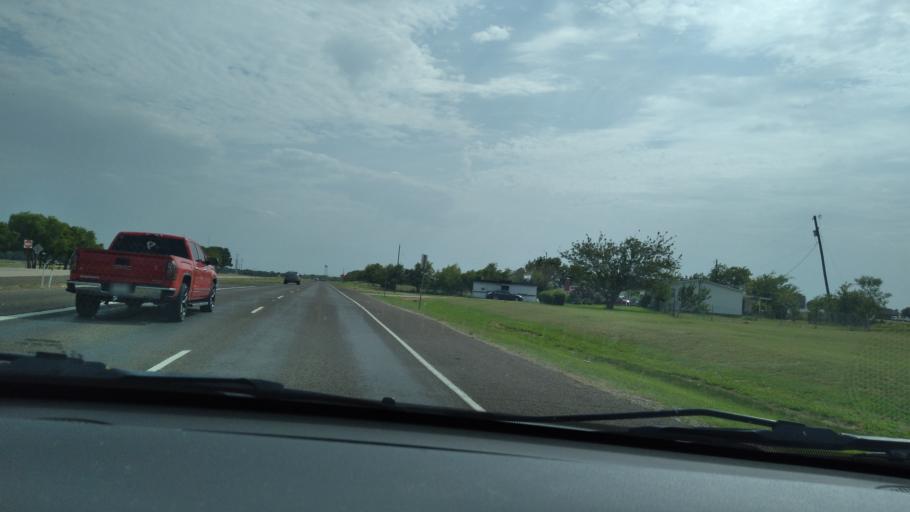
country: US
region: Texas
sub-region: Navarro County
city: Corsicana
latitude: 32.0493
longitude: -96.5353
